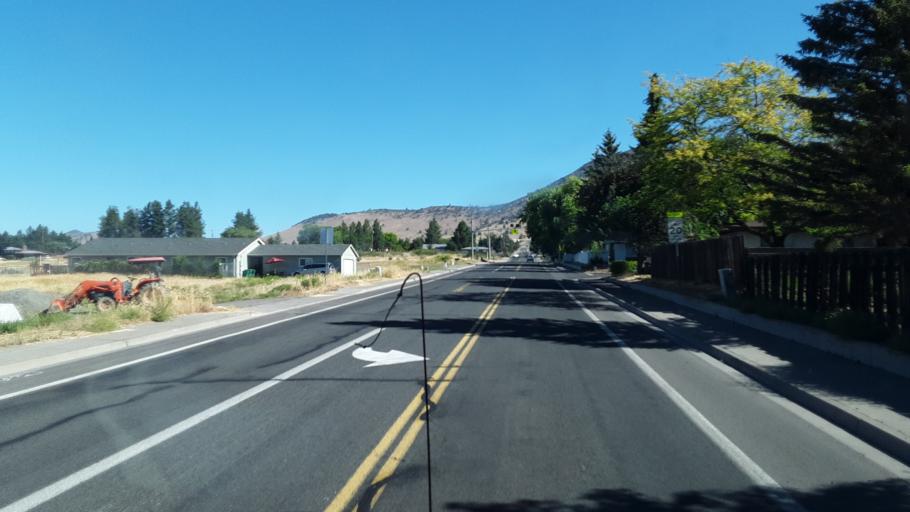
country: US
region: Oregon
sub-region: Klamath County
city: Altamont
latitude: 42.2108
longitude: -121.7129
